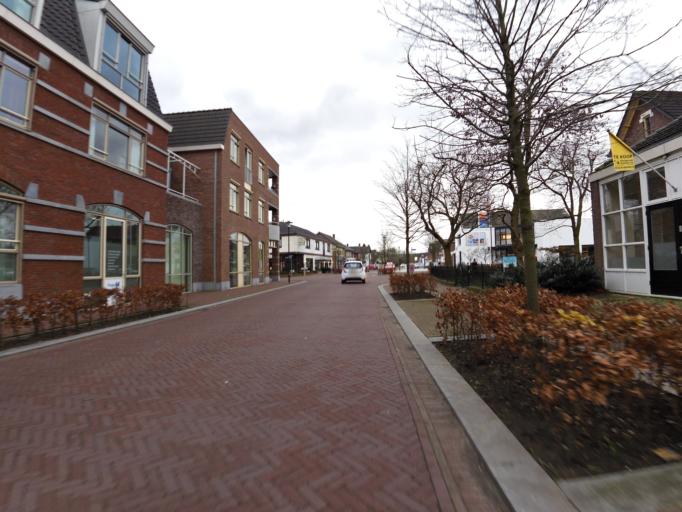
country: NL
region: Gelderland
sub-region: Gemeente Montferland
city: s-Heerenberg
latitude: 51.9033
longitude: 6.2577
